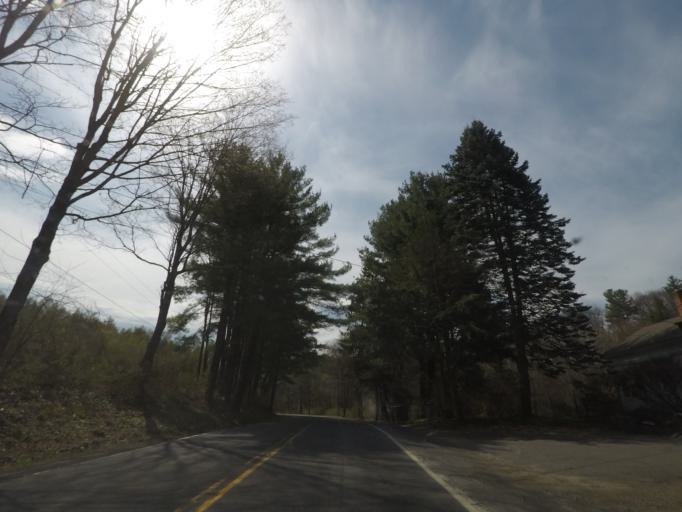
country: US
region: New York
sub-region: Columbia County
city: Chatham
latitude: 42.3451
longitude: -73.5858
